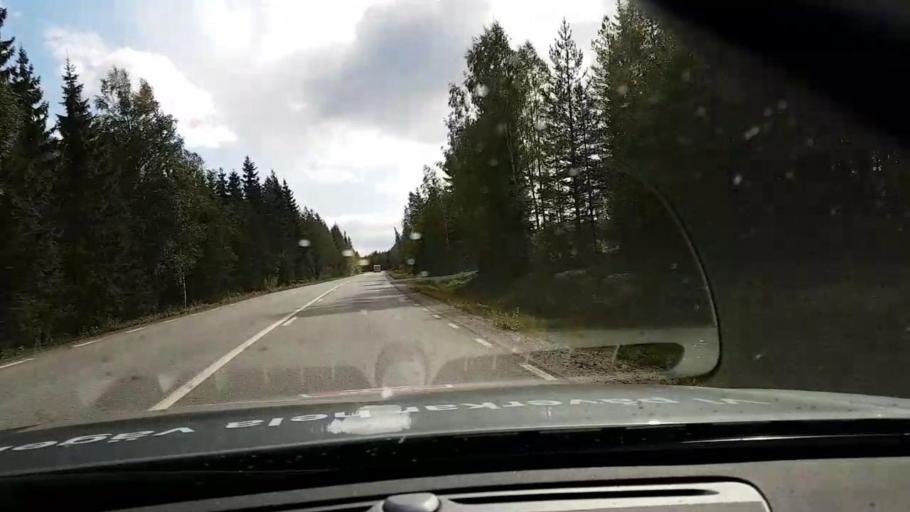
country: SE
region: Vaesternorrland
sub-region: OErnskoeldsviks Kommun
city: Bredbyn
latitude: 63.6288
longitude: 17.9105
